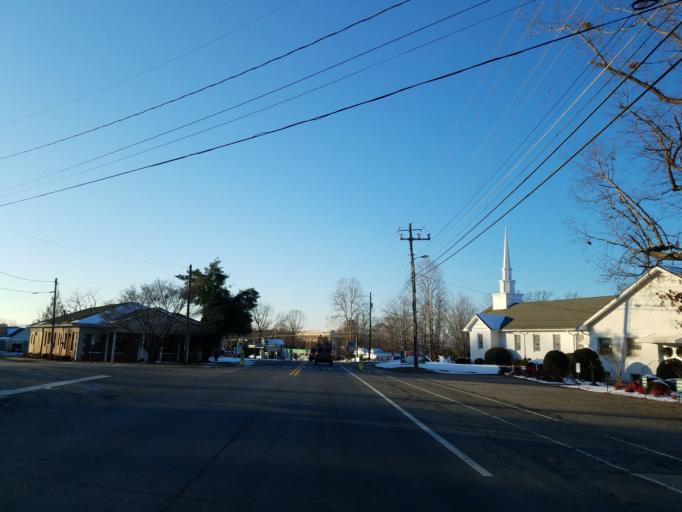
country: US
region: Georgia
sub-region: Dawson County
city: Dawsonville
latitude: 34.4205
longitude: -84.1156
